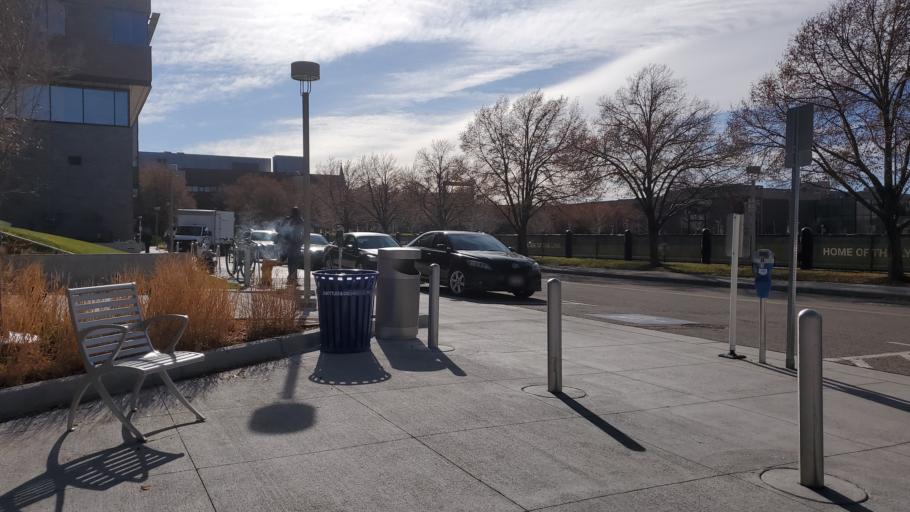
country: US
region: Colorado
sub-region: Denver County
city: Denver
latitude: 39.7466
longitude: -105.0030
